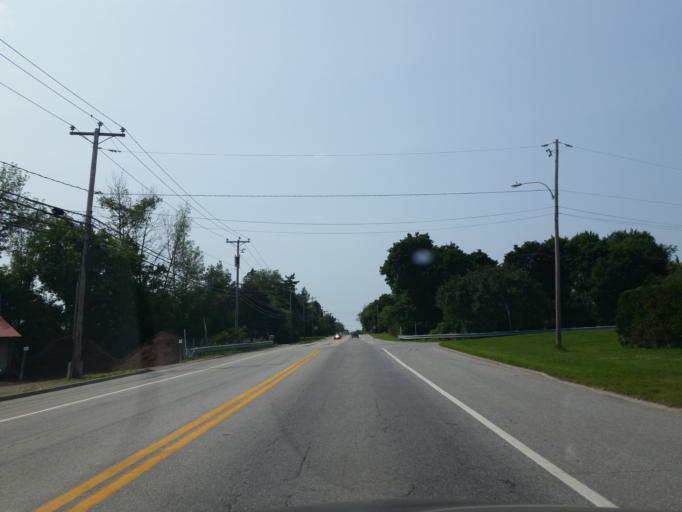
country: CA
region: Ontario
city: Bells Corners
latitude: 45.4109
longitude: -75.8713
